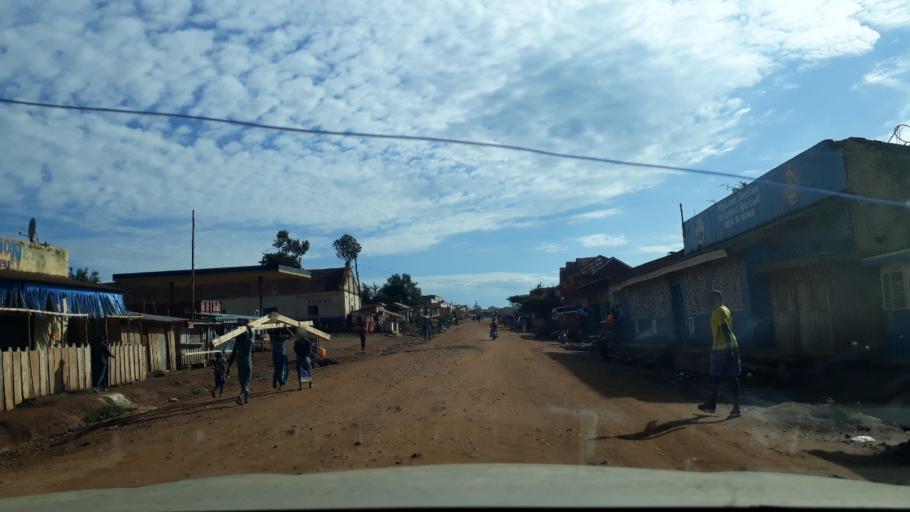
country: UG
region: Northern Region
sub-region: Zombo District
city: Paidha
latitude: 2.2983
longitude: 30.9888
